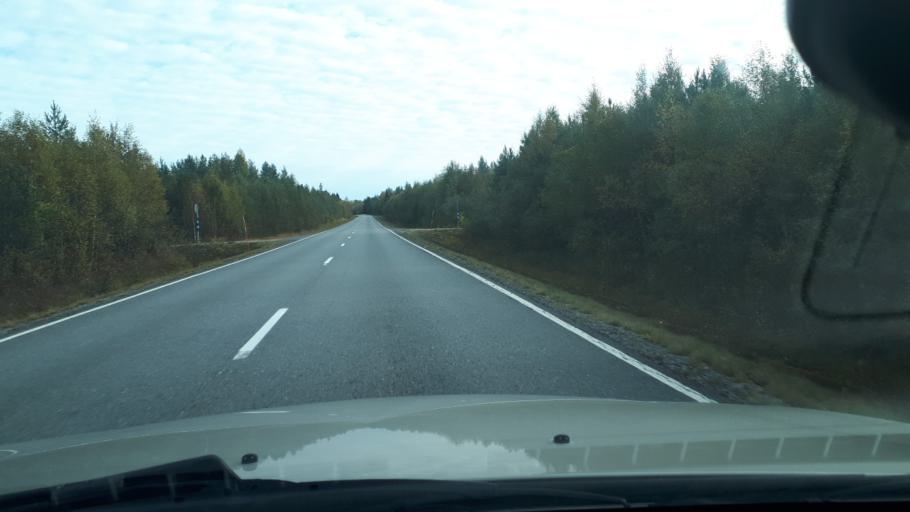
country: FI
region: Northern Ostrobothnia
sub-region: Oulu
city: Yli-Ii
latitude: 65.9265
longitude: 25.8369
